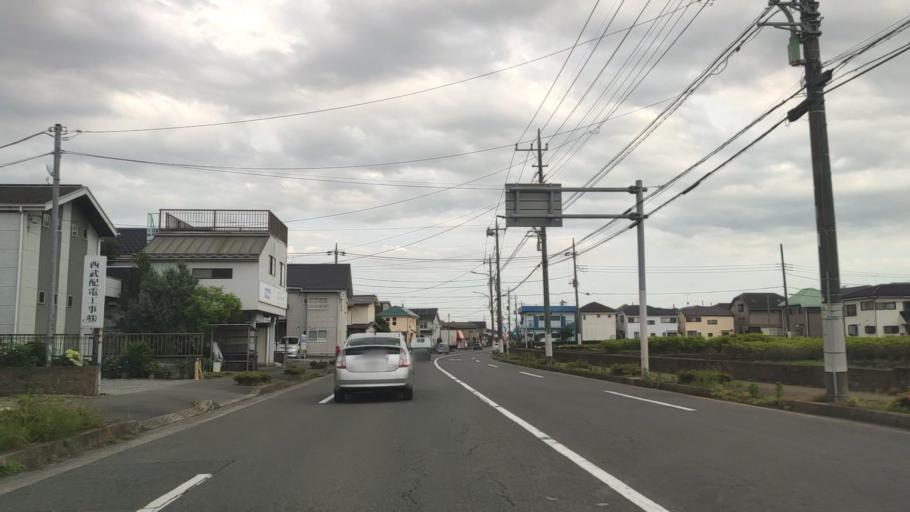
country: JP
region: Tokyo
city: Ome
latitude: 35.7957
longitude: 139.2984
